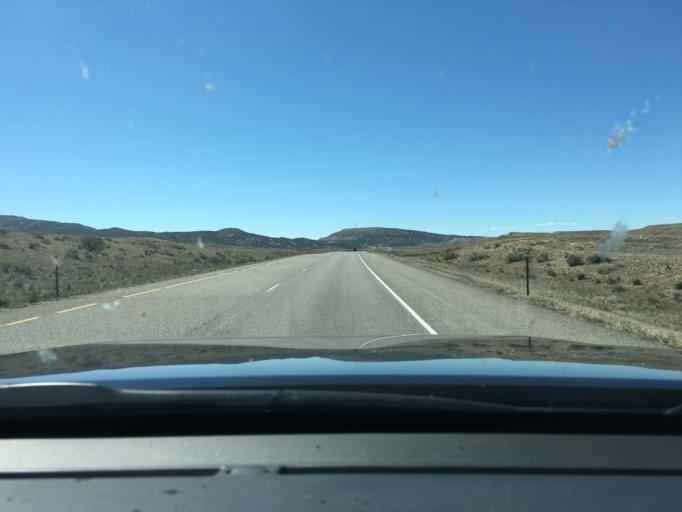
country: US
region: Colorado
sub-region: Mesa County
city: Loma
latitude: 39.2297
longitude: -108.9194
